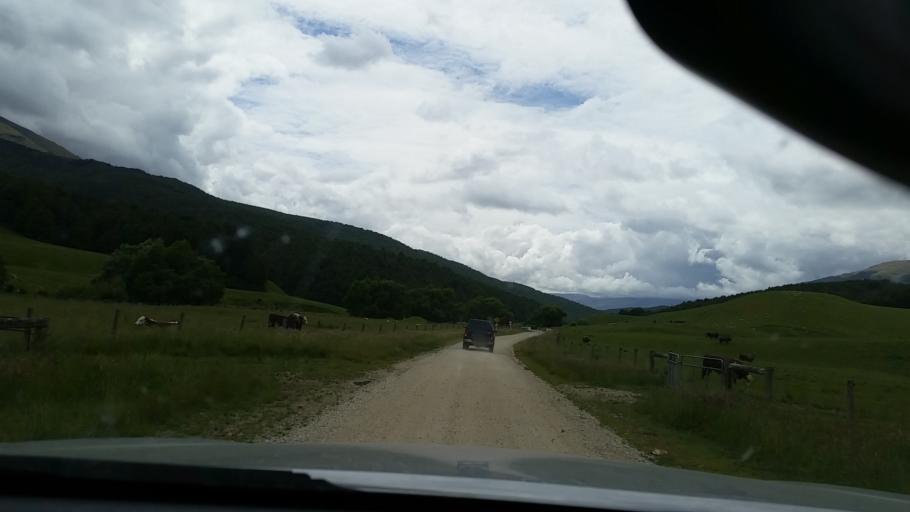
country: NZ
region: Otago
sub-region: Queenstown-Lakes District
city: Kingston
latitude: -45.5758
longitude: 169.0015
